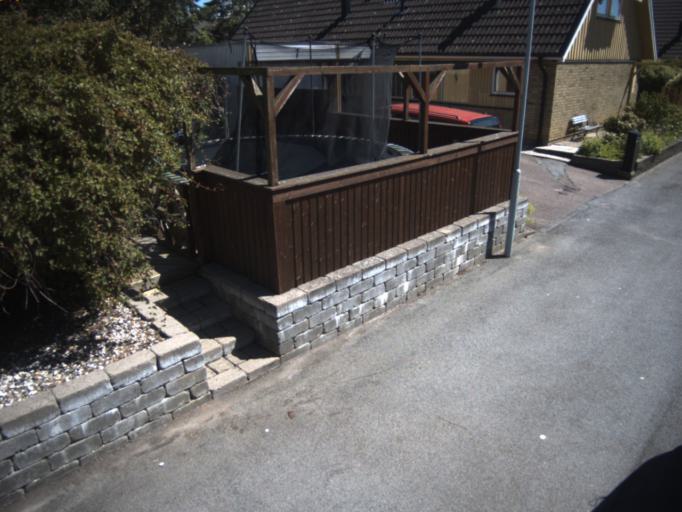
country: SE
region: Skane
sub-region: Helsingborg
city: Rydeback
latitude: 55.9689
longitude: 12.7748
